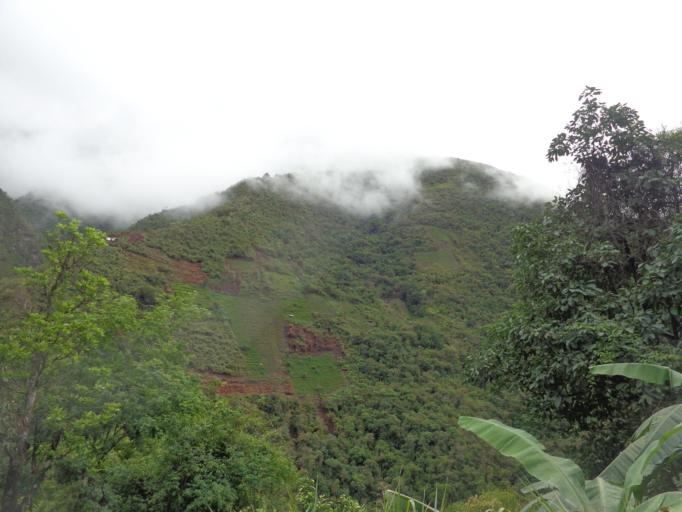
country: BO
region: La Paz
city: Coripata
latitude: -16.3932
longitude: -67.6800
